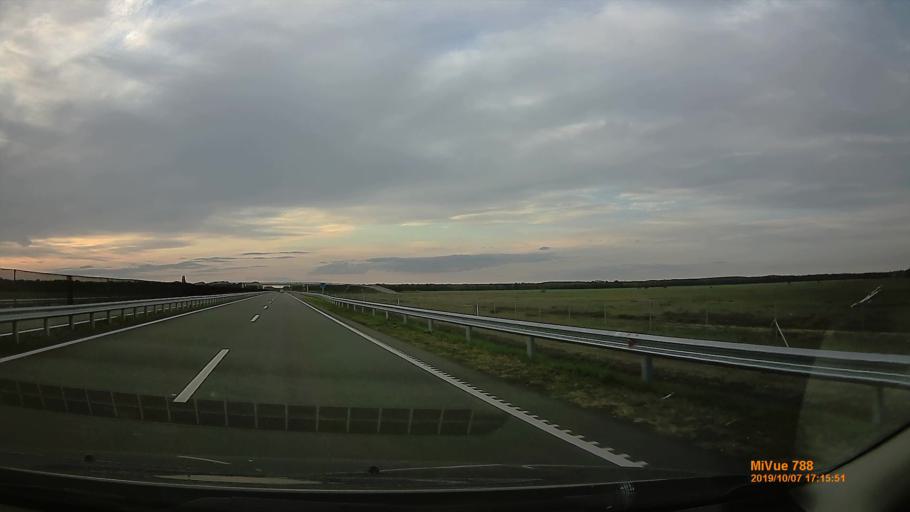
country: HU
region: Jasz-Nagykun-Szolnok
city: Kunszentmarton
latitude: 46.8505
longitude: 20.3210
